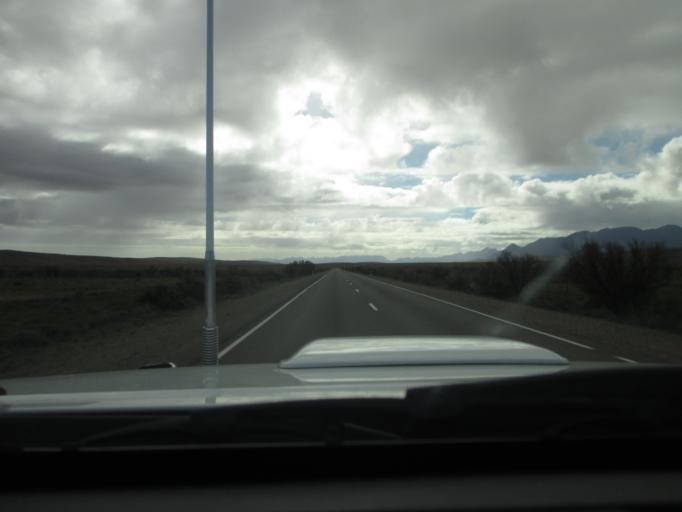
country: AU
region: South Australia
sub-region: Flinders Ranges
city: Quorn
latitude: -31.6098
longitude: 138.3984
